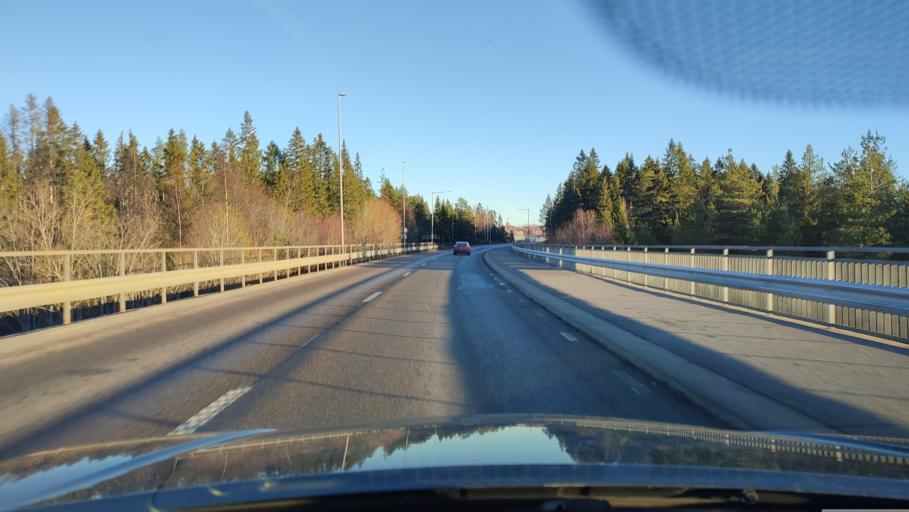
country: SE
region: Vaesterbotten
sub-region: Umea Kommun
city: Holmsund
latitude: 63.7122
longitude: 20.3430
